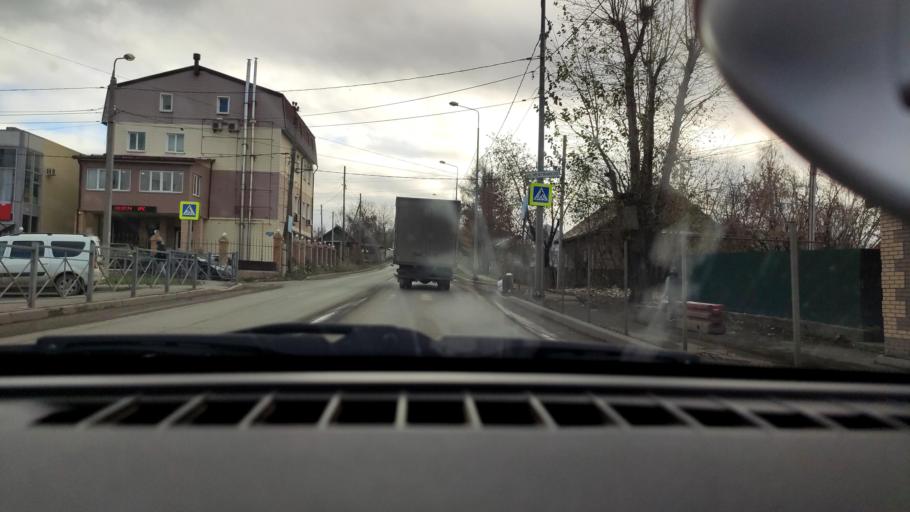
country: RU
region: Perm
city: Kondratovo
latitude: 57.9665
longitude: 56.1519
